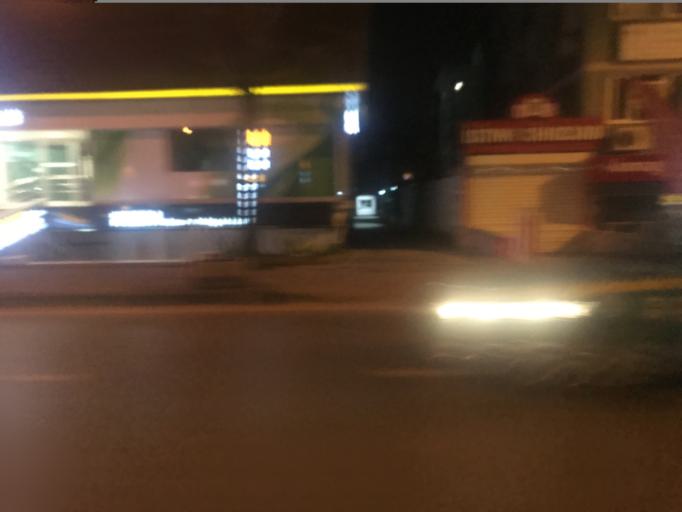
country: TR
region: Istanbul
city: Bahcelievler
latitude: 40.9875
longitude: 28.8721
